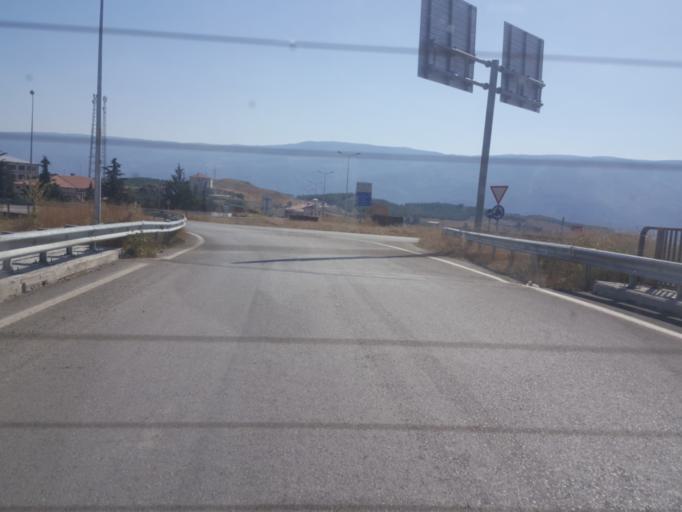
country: TR
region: Kastamonu
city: Tosya
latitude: 41.0076
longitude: 34.0588
